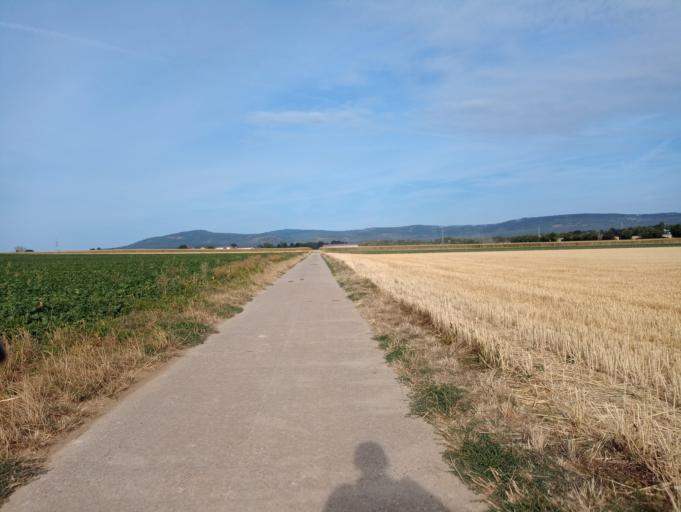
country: DE
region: Hesse
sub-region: Regierungsbezirk Darmstadt
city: Bad Homburg vor der Hoehe
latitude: 50.2029
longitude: 8.6232
